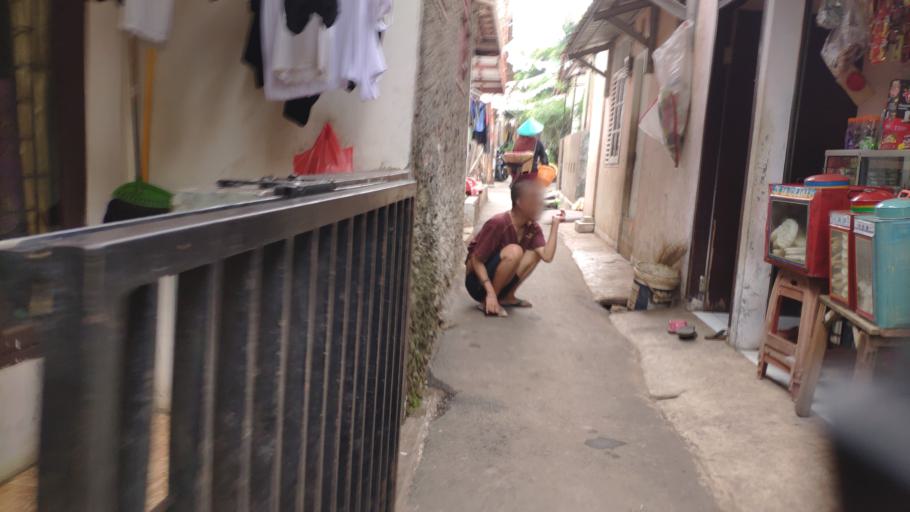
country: ID
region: West Java
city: Depok
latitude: -6.3116
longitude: 106.8298
